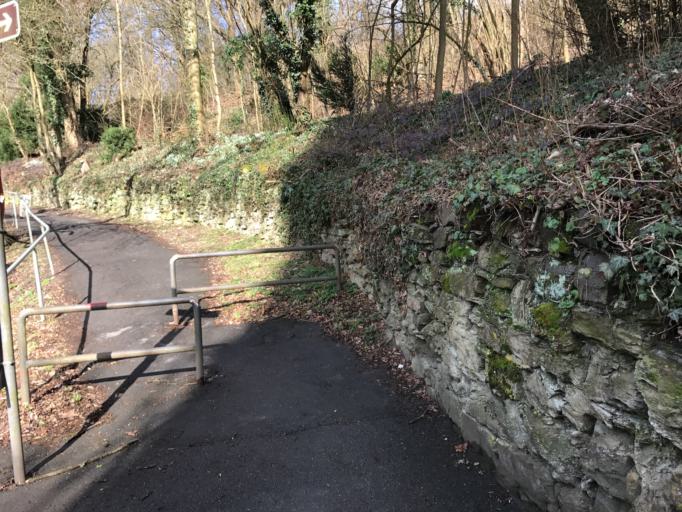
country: DE
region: Hesse
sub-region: Regierungsbezirk Darmstadt
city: Wiesbaden
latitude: 50.1002
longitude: 8.2673
